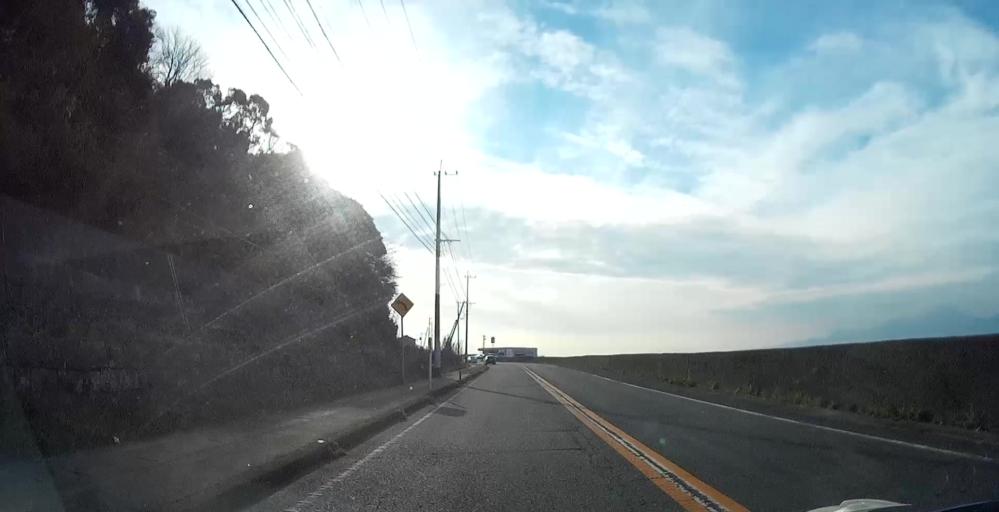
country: JP
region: Kumamoto
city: Uto
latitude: 32.6887
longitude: 130.5565
